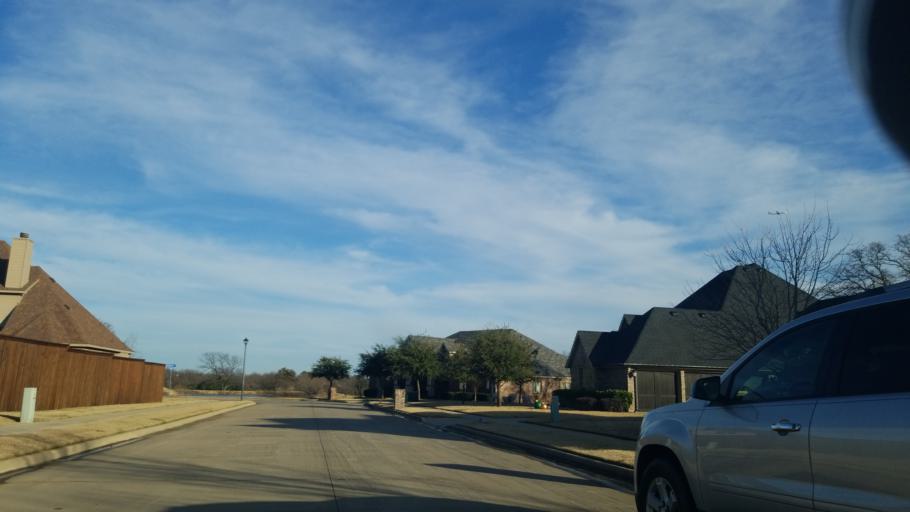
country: US
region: Texas
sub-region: Denton County
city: Corinth
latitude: 33.1510
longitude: -97.0743
